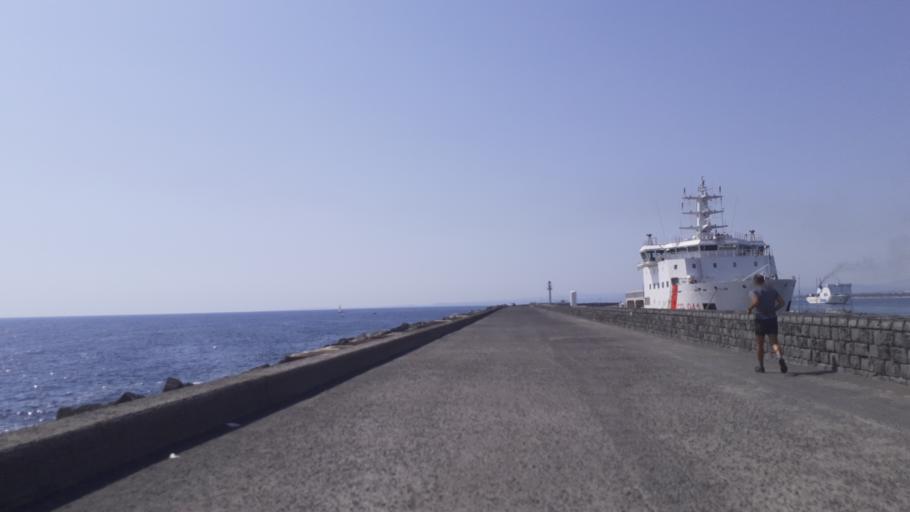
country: IT
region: Sicily
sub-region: Catania
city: Catania
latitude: 37.4951
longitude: 15.0996
